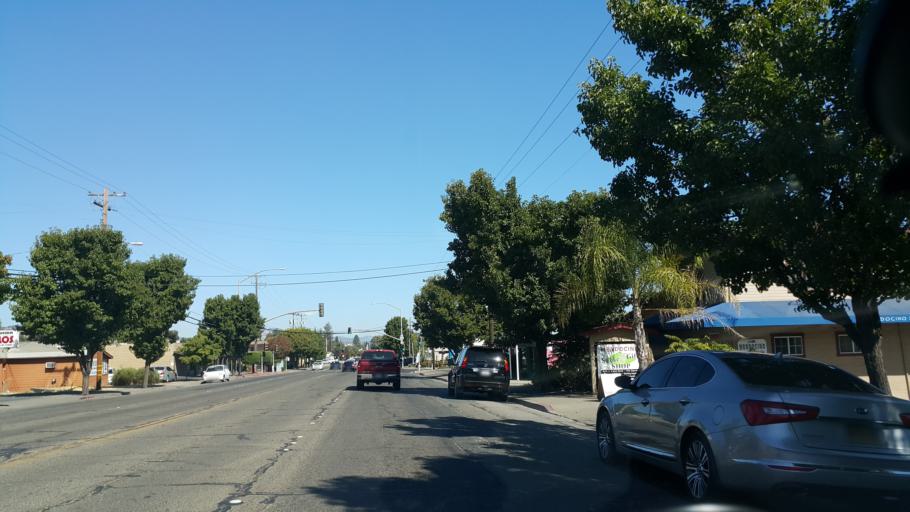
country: US
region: California
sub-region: Mendocino County
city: Ukiah
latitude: 39.1353
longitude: -123.2052
